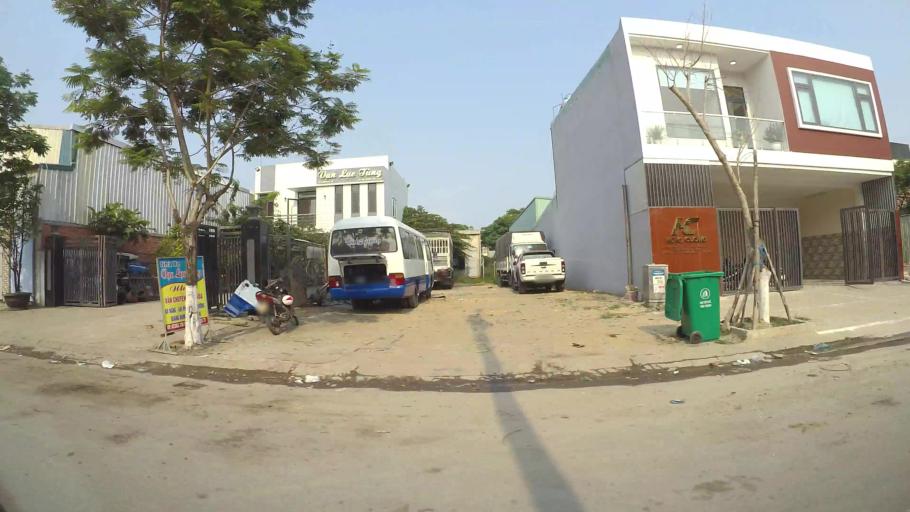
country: VN
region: Da Nang
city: Thanh Khe
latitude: 16.0504
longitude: 108.1743
